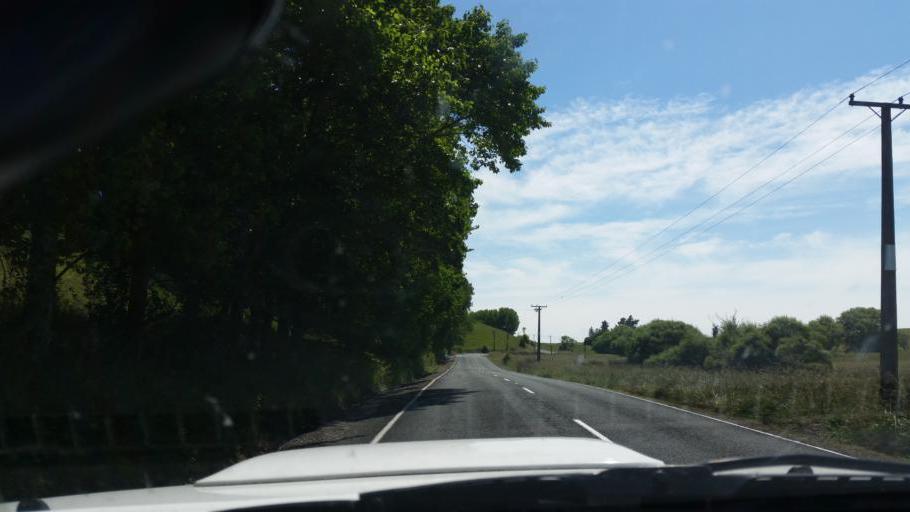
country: NZ
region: Auckland
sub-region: Auckland
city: Wellsford
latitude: -36.1918
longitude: 174.4030
